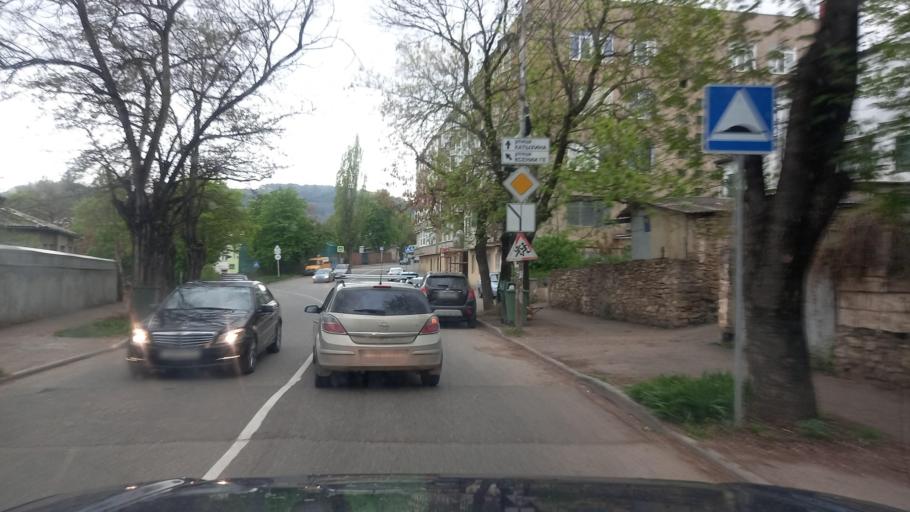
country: RU
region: Stavropol'skiy
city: Kislovodsk
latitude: 43.8991
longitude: 42.7116
